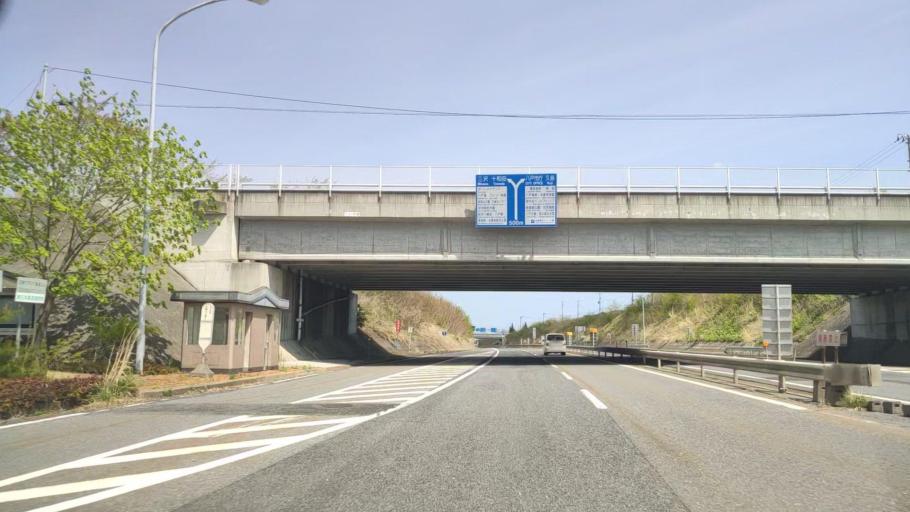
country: JP
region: Aomori
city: Hachinohe
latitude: 40.4871
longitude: 141.4631
